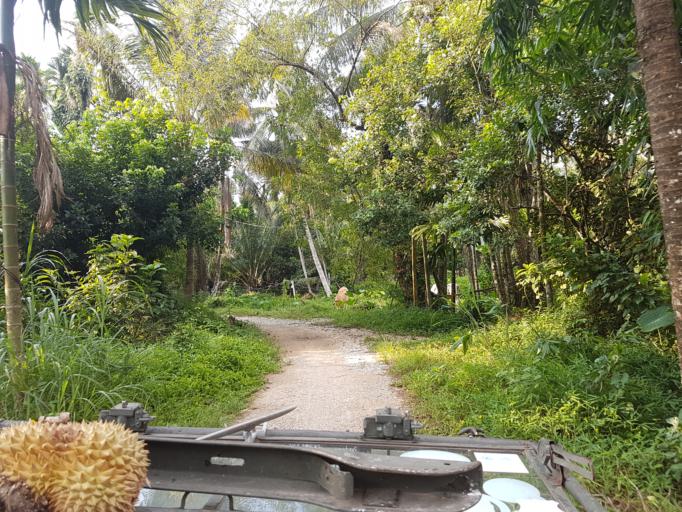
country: TH
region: Pattani
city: Khok Pho
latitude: 6.6645
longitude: 101.0886
